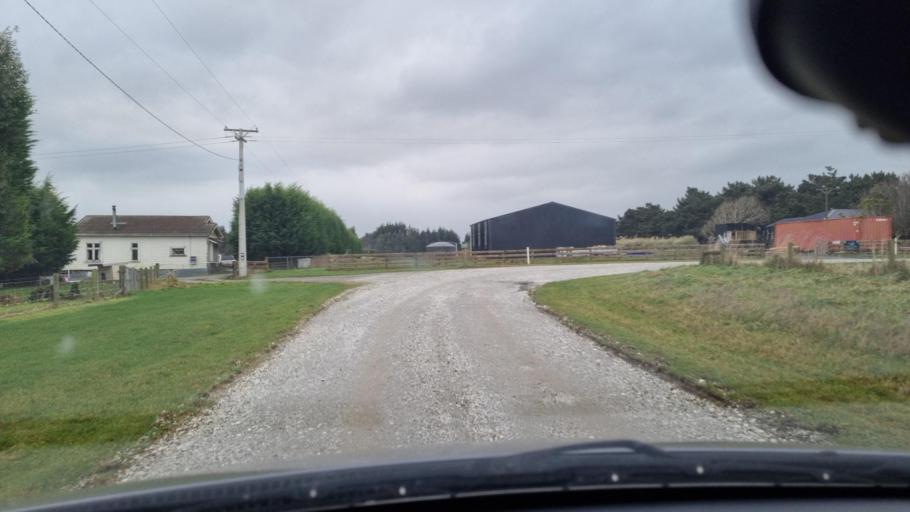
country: NZ
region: Southland
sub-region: Invercargill City
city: Invercargill
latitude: -46.4326
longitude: 168.4100
